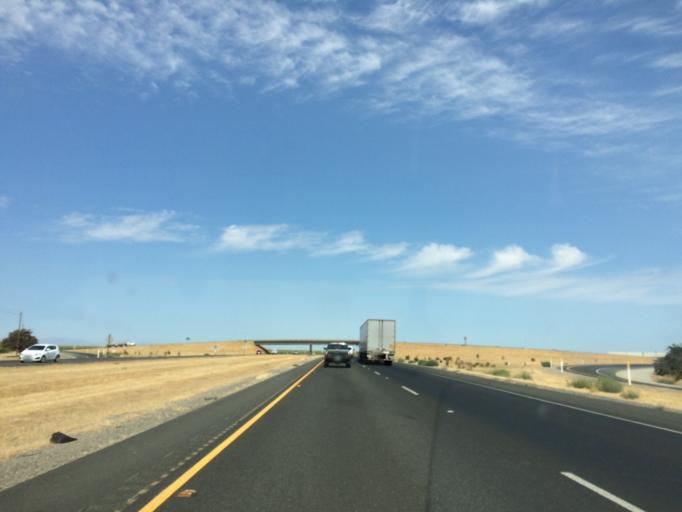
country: US
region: California
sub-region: Yolo County
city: Dunnigan
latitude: 38.9230
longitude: -121.9985
